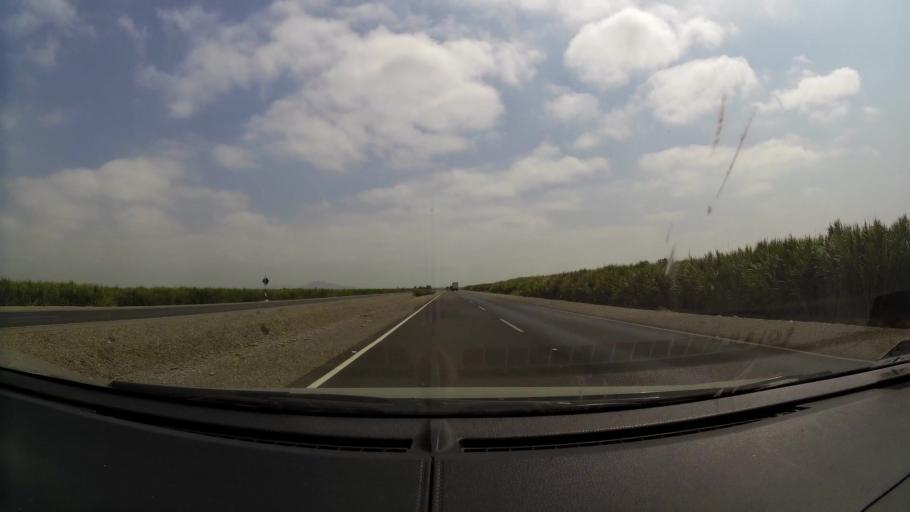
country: PE
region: La Libertad
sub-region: Ascope
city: Chicama
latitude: -7.8488
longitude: -79.1498
